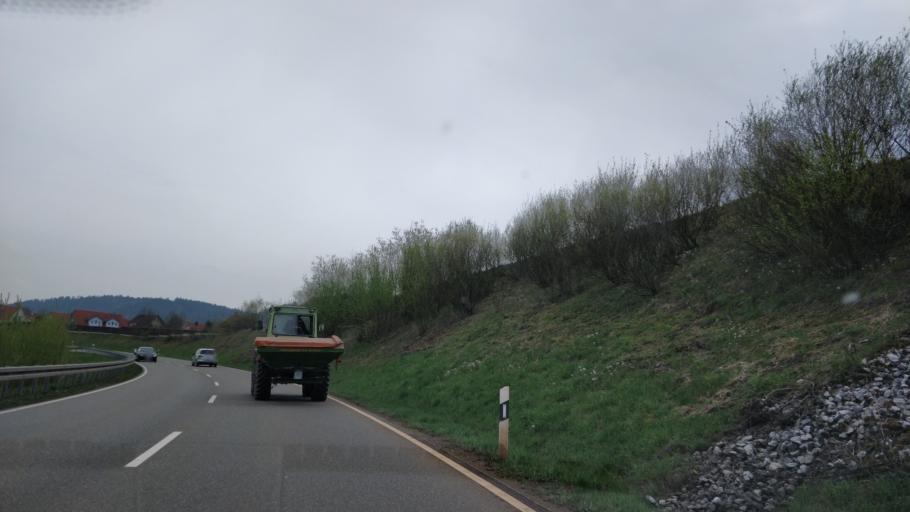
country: DE
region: Baden-Wuerttemberg
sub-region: Regierungsbezirk Stuttgart
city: Fichtenberg
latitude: 48.9843
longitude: 9.7033
